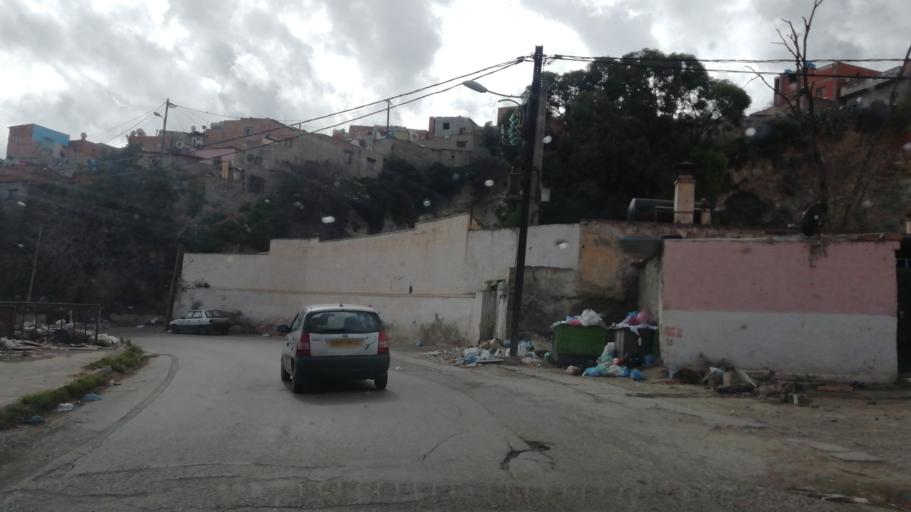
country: DZ
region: Oran
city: Oran
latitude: 35.6983
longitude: -0.6618
